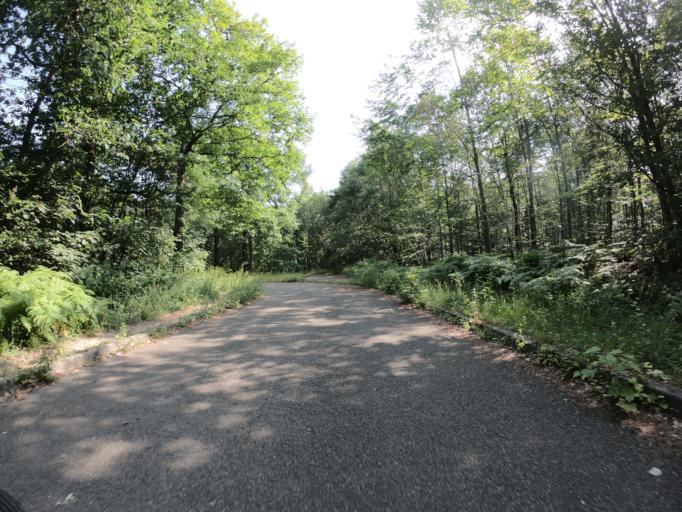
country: FR
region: Ile-de-France
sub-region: Departement de l'Essonne
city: Igny
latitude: 48.7528
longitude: 2.2358
